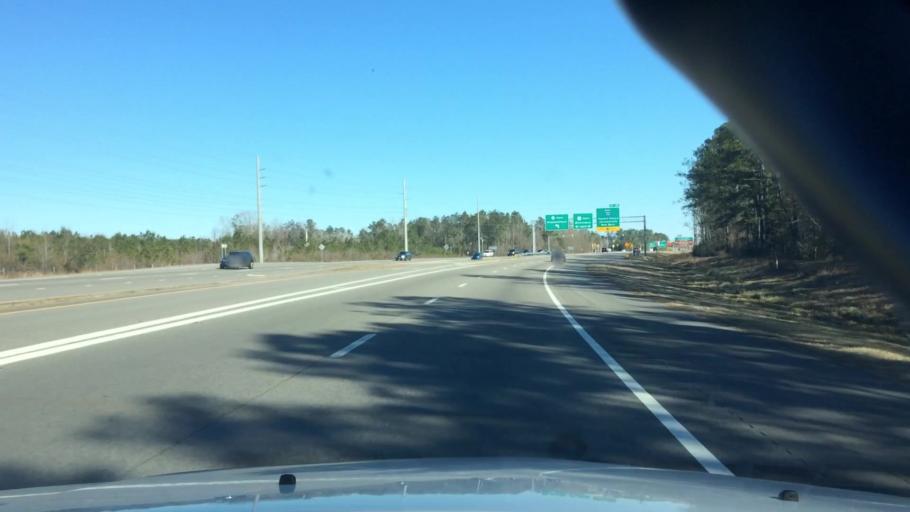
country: US
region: North Carolina
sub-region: Brunswick County
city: Leland
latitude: 34.1764
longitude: -78.0863
